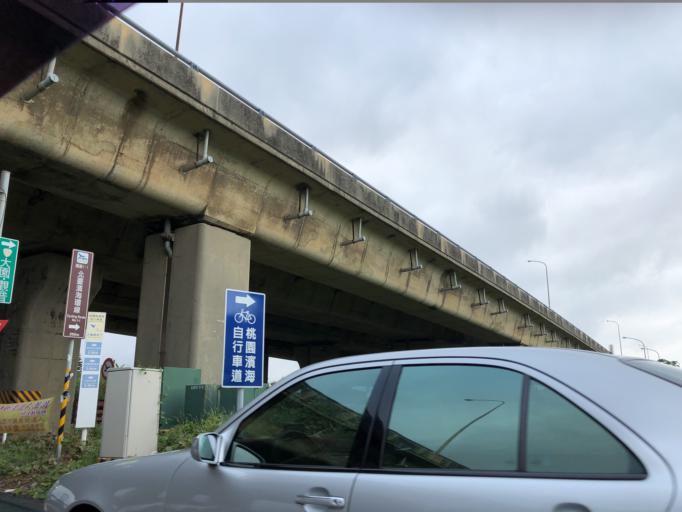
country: TW
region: Taiwan
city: Taoyuan City
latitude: 25.1136
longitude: 121.2429
